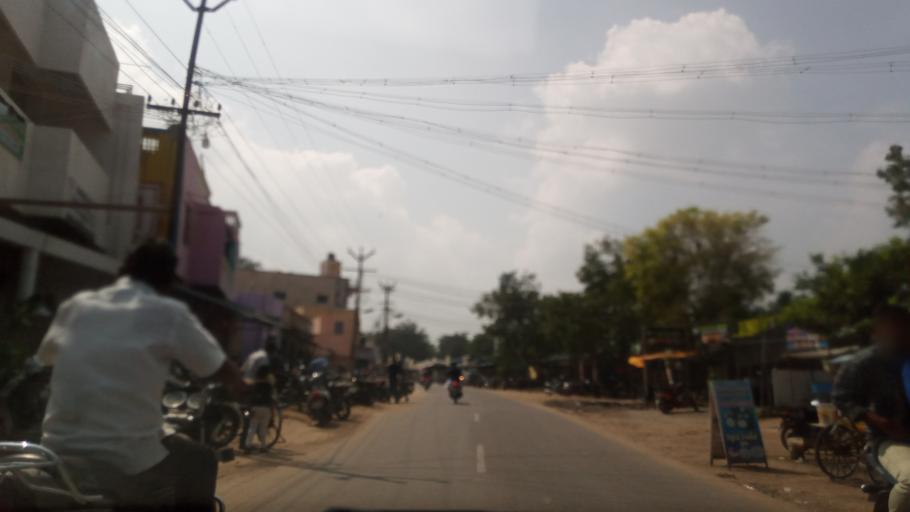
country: IN
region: Tamil Nadu
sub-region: Vellore
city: Arakkonam
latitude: 13.0772
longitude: 79.6714
